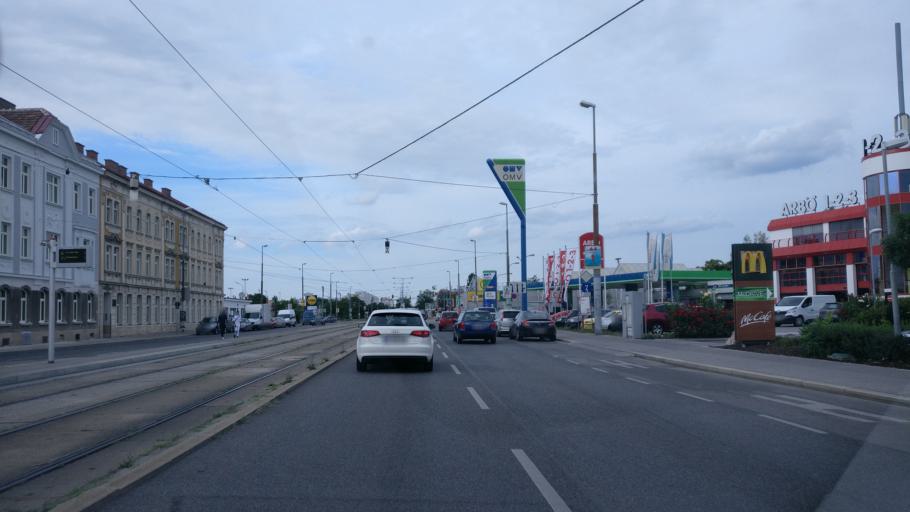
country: AT
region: Lower Austria
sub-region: Politischer Bezirk Korneuburg
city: Hagenbrunn
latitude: 48.2804
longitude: 16.4111
